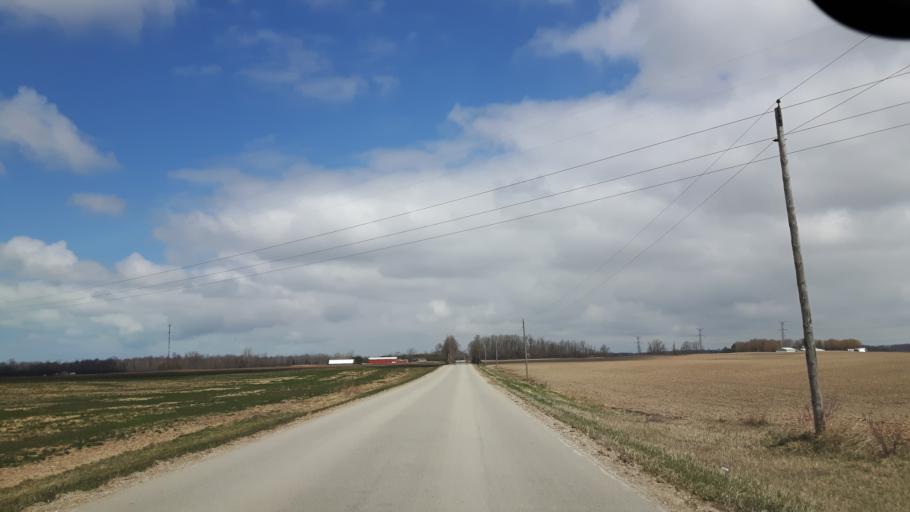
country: CA
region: Ontario
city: Goderich
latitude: 43.6999
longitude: -81.6645
